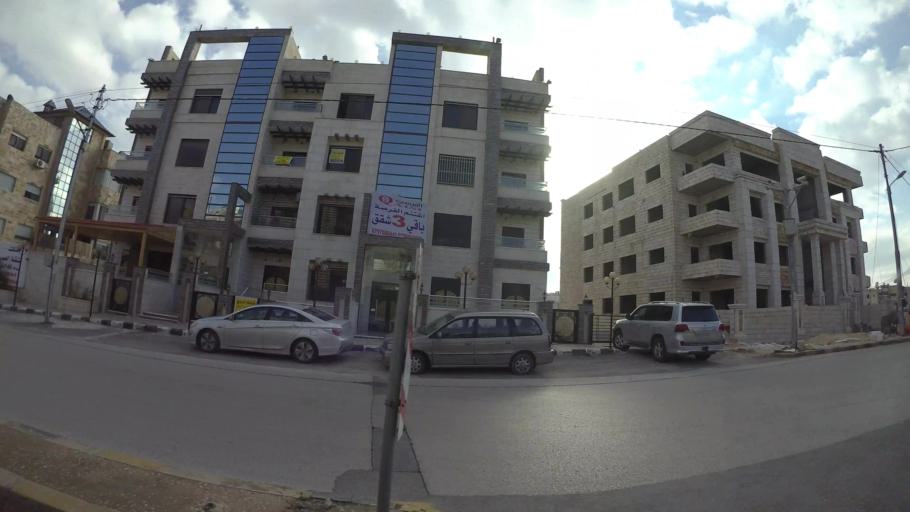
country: JO
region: Amman
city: Al Jubayhah
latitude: 31.9792
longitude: 35.8845
